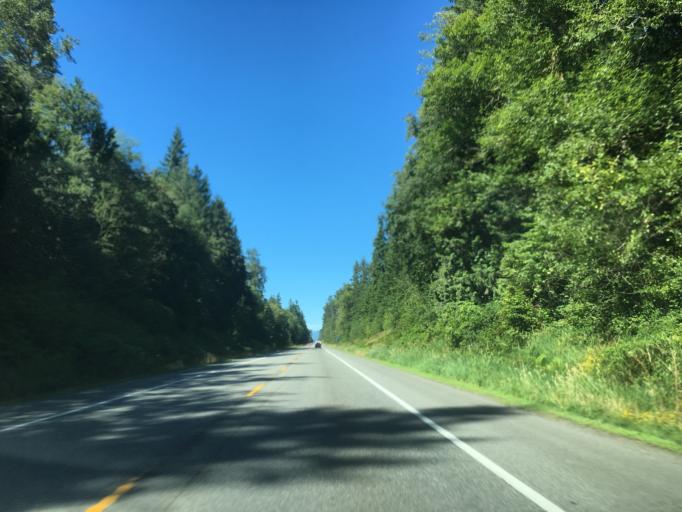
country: US
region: Washington
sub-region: Snohomish County
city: Sisco Heights
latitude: 48.1059
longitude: -122.1121
